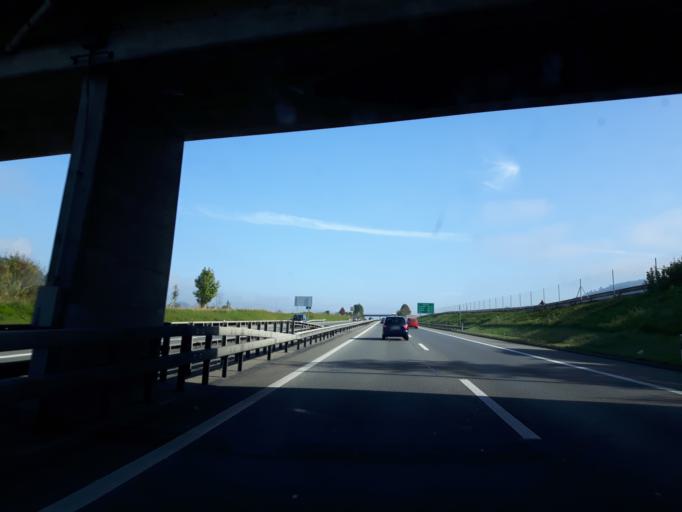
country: CH
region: Lucerne
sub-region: Willisau District
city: Dagmersellen
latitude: 47.2078
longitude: 7.9872
